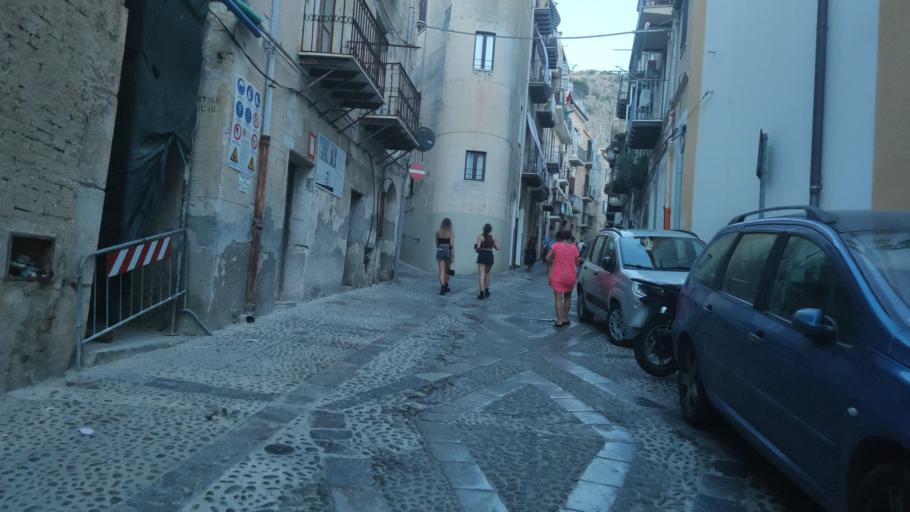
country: IT
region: Sicily
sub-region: Palermo
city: Cefalu
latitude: 38.0381
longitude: 14.0202
